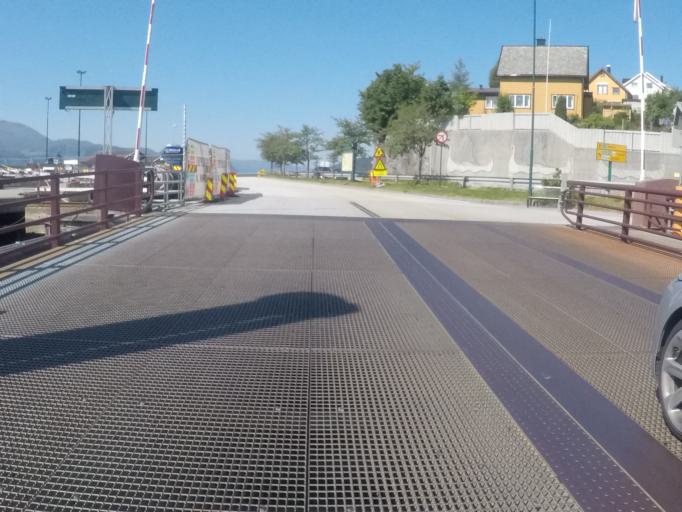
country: NO
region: More og Romsdal
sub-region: Volda
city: Volda
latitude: 62.1447
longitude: 6.0637
